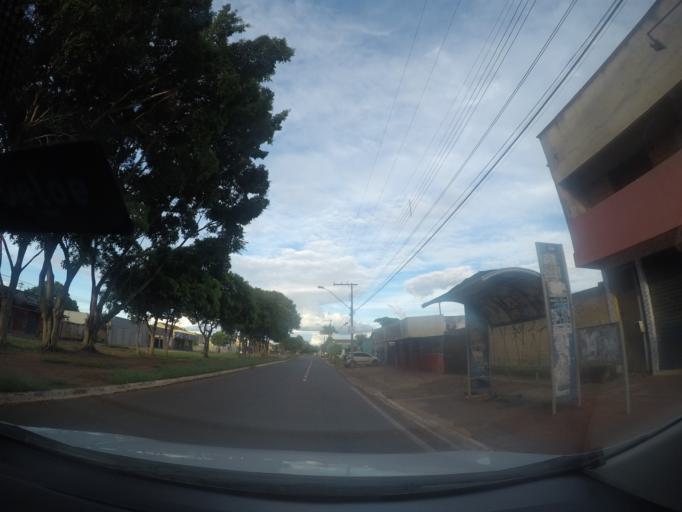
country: BR
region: Goias
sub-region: Goianira
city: Goianira
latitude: -16.5888
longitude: -49.3747
